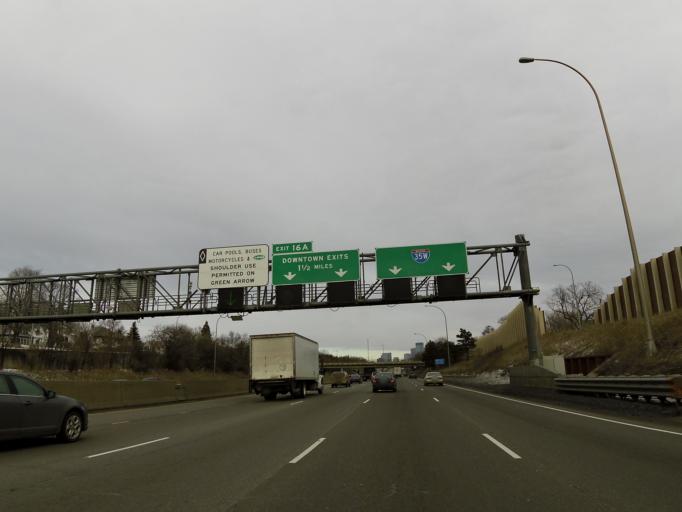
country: US
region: Minnesota
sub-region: Hennepin County
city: Minneapolis
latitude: 44.9356
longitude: -93.2745
